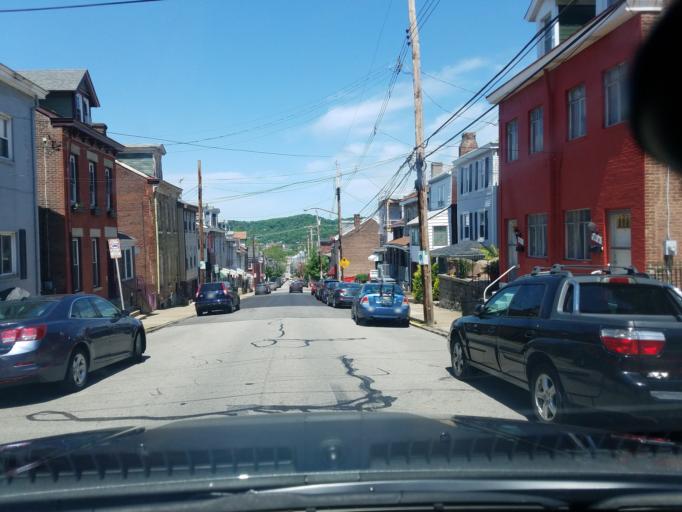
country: US
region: Pennsylvania
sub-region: Allegheny County
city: Bloomfield
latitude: 40.4699
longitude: -79.9562
